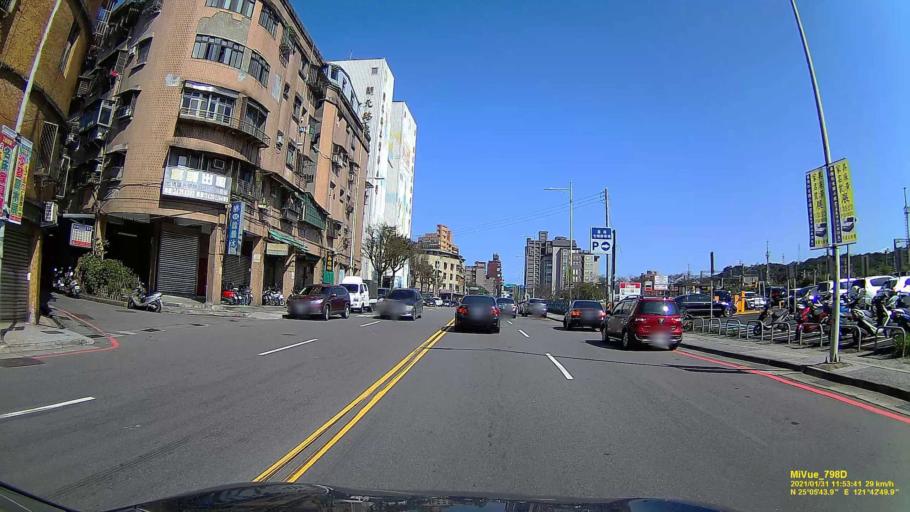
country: TW
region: Taiwan
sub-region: Keelung
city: Keelung
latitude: 25.0956
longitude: 121.7140
